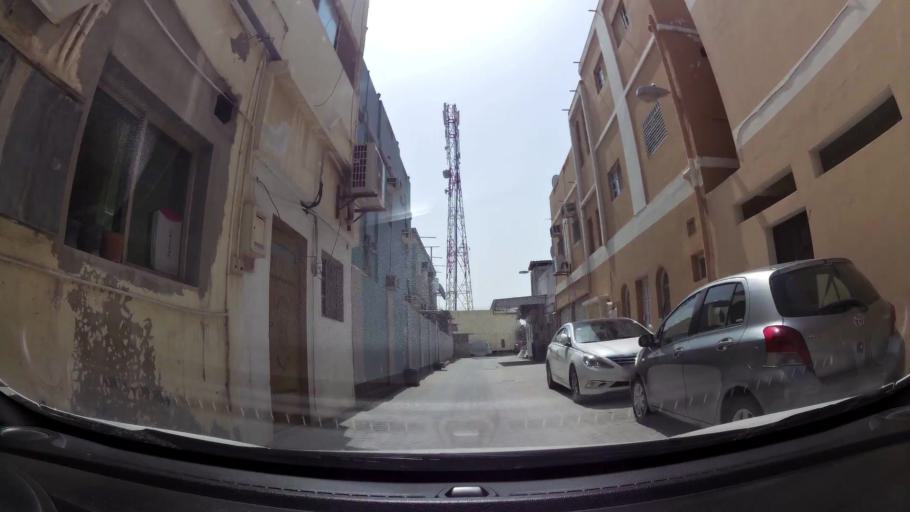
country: BH
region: Manama
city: Jidd Hafs
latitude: 26.2277
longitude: 50.4785
